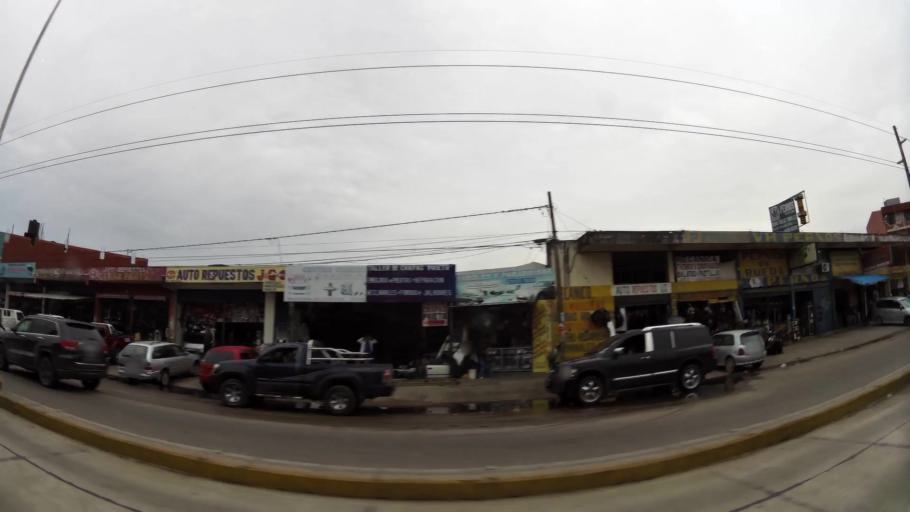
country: BO
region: Santa Cruz
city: Santa Cruz de la Sierra
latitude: -17.8090
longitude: -63.1942
